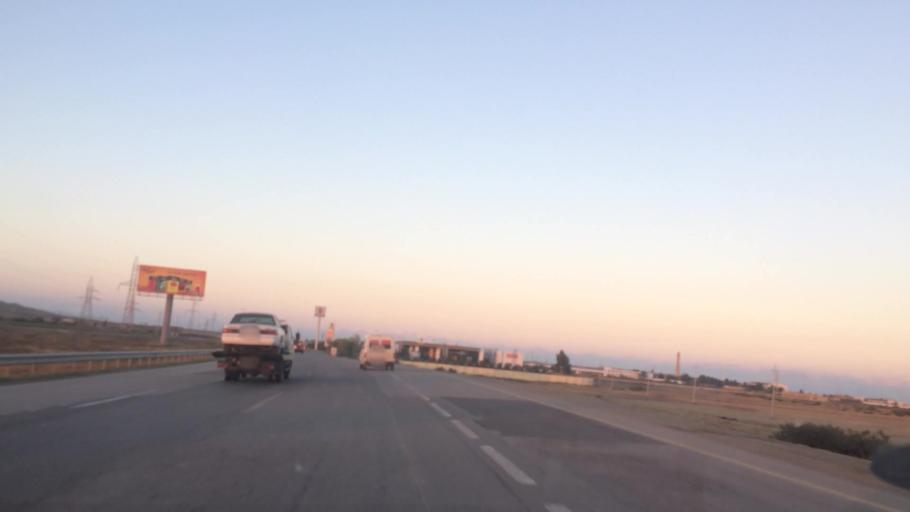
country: AZ
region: Baki
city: Qobustan
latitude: 39.9680
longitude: 49.4132
